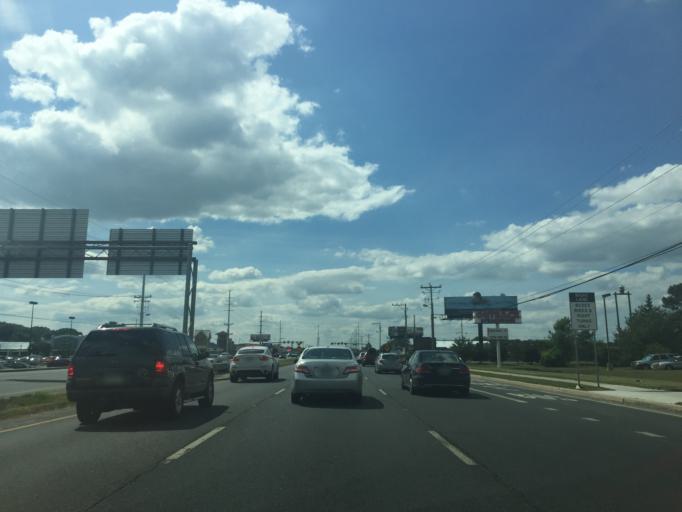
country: US
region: Delaware
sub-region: Sussex County
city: Rehoboth Beach
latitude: 38.7153
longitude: -75.1077
